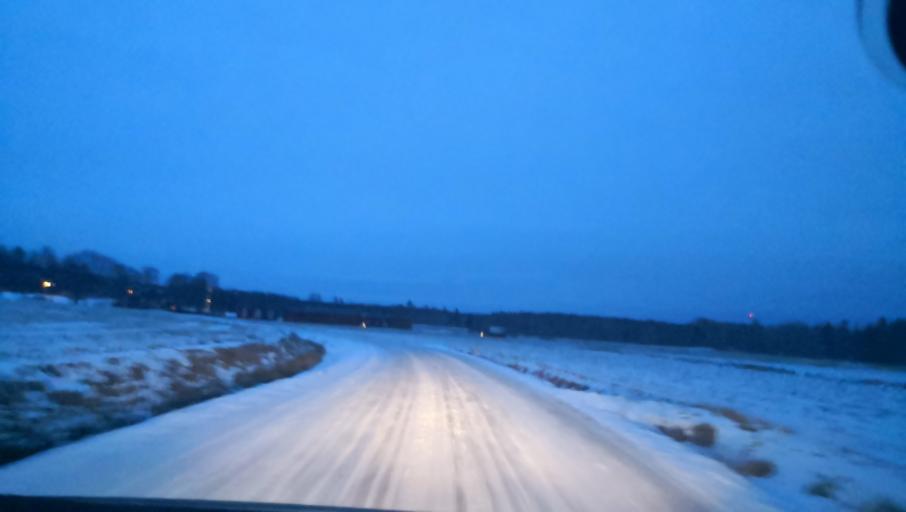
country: SE
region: Uppsala
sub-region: Heby Kommun
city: Tarnsjo
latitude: 60.2417
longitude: 16.6810
